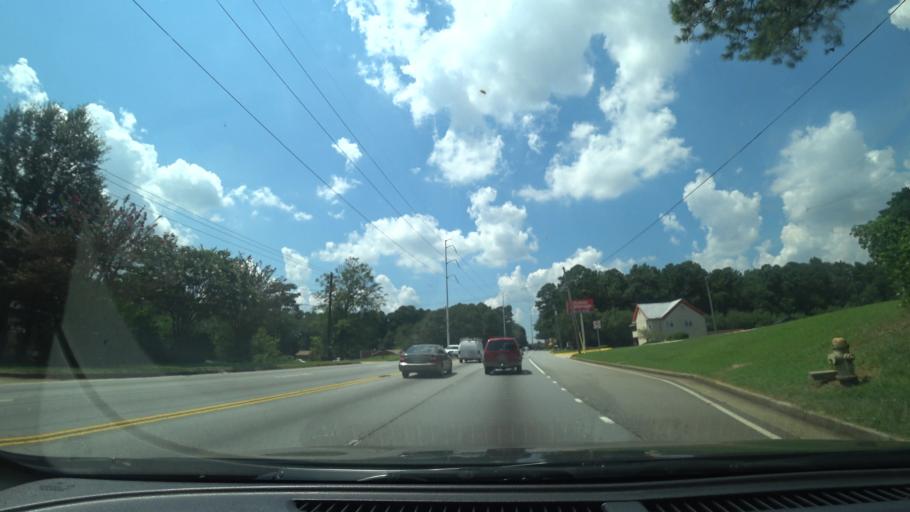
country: US
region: Georgia
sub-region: DeKalb County
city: Belvedere Park
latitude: 33.7333
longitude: -84.2081
